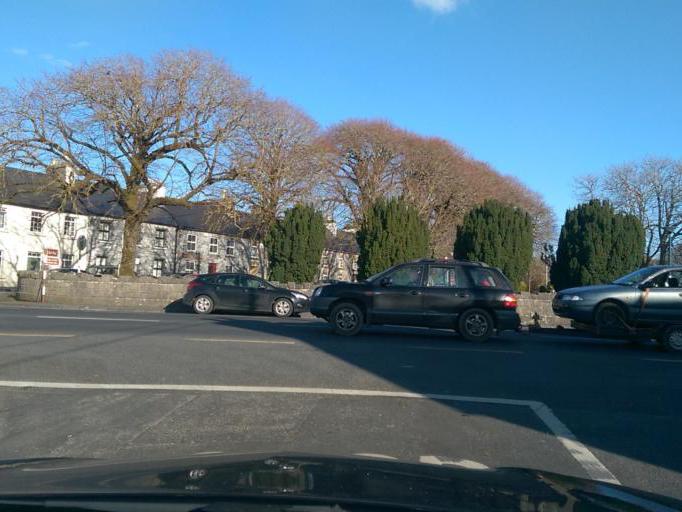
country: IE
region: Connaught
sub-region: County Galway
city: Oranmore
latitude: 53.2293
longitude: -8.8810
